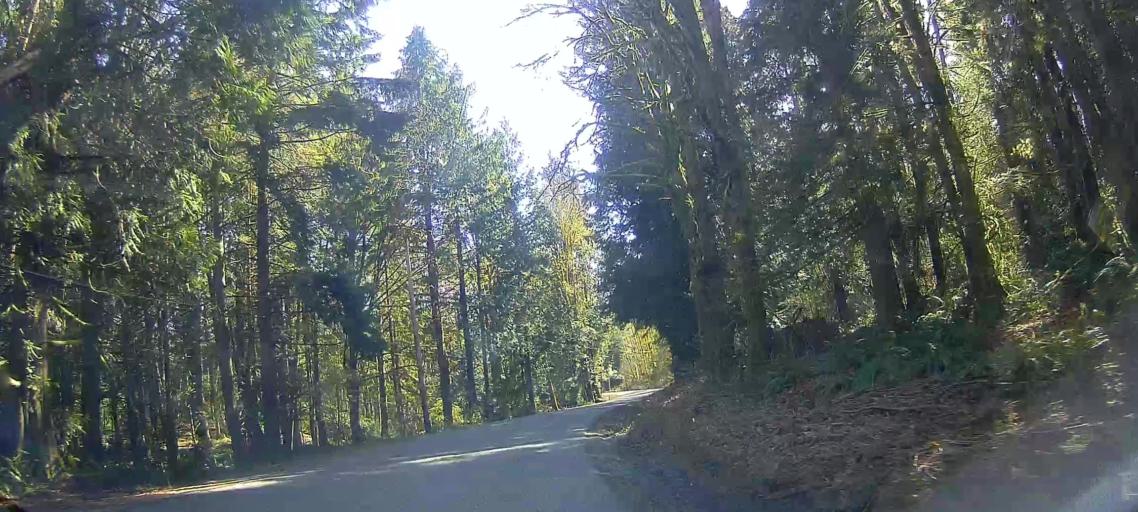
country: US
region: Washington
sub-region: Whatcom County
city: Sudden Valley
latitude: 48.6171
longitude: -122.3682
